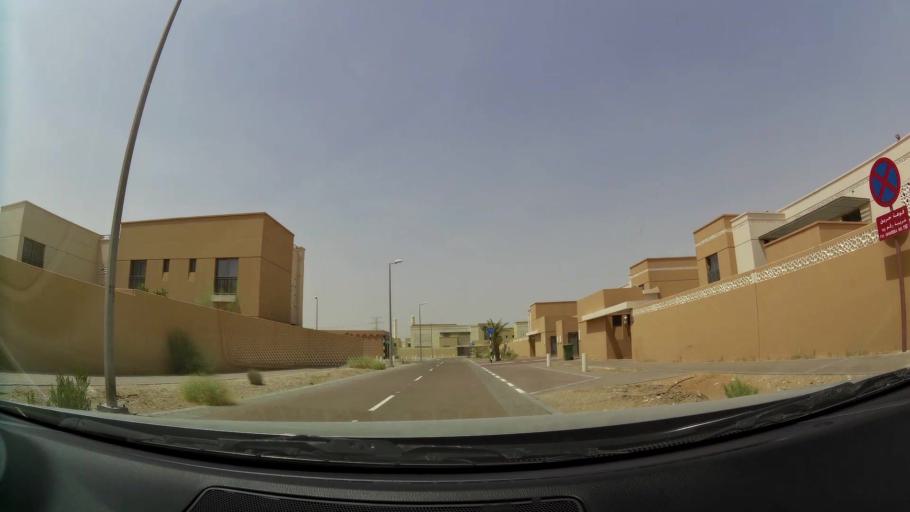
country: AE
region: Abu Dhabi
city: Al Ain
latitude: 24.1418
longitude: 55.6192
